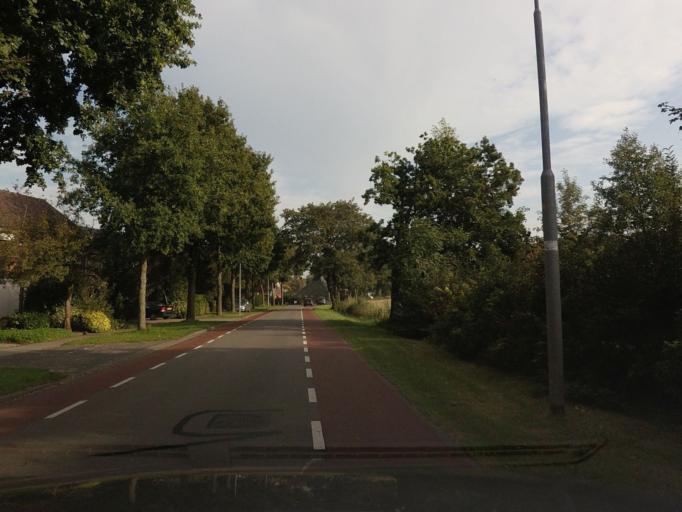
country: NL
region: North Holland
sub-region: Gemeente Schagen
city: Harenkarspel
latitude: 52.7083
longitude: 4.6993
